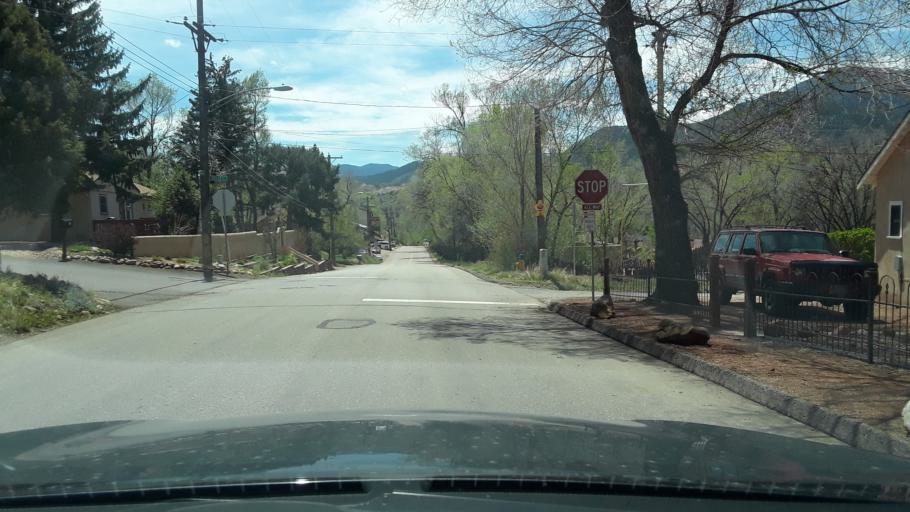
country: US
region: Colorado
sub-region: El Paso County
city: Manitou Springs
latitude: 38.8611
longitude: -104.8848
